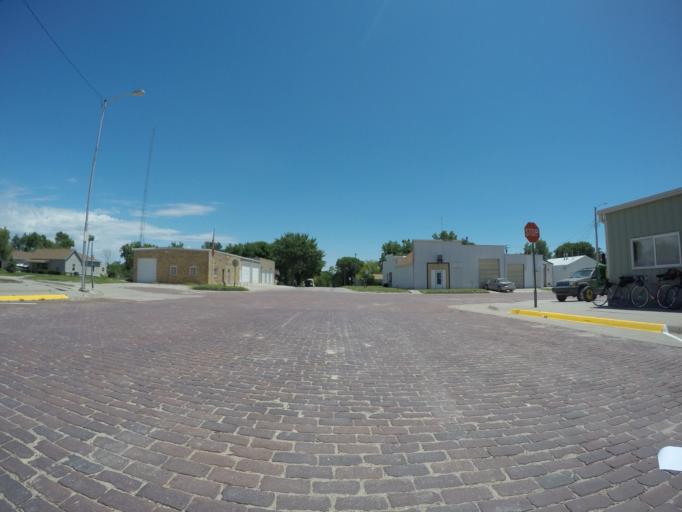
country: US
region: Kansas
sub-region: Jewell County
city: Mankato
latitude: 39.7867
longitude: -98.2084
